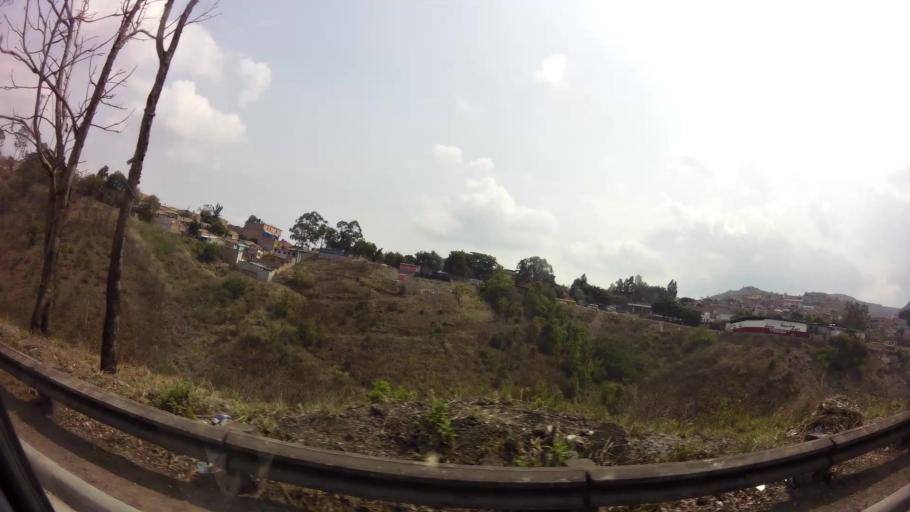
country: HN
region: Francisco Morazan
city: Tegucigalpa
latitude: 14.1207
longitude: -87.2227
